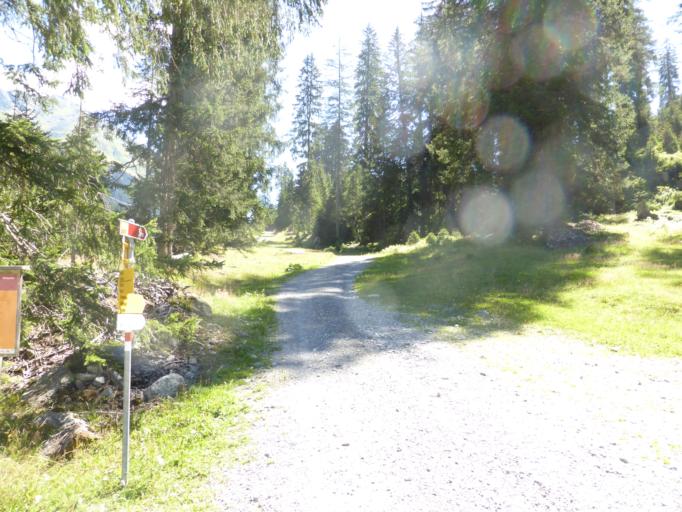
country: CH
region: Grisons
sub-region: Praettigau/Davos District
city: Klosters Serneus
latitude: 46.8589
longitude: 9.9301
